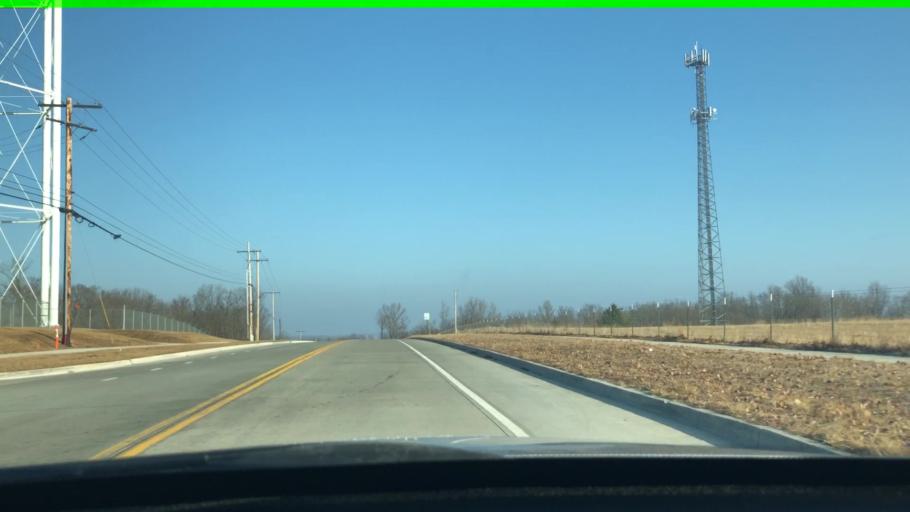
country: US
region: Missouri
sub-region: Boone County
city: Columbia
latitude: 38.8961
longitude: -92.4005
